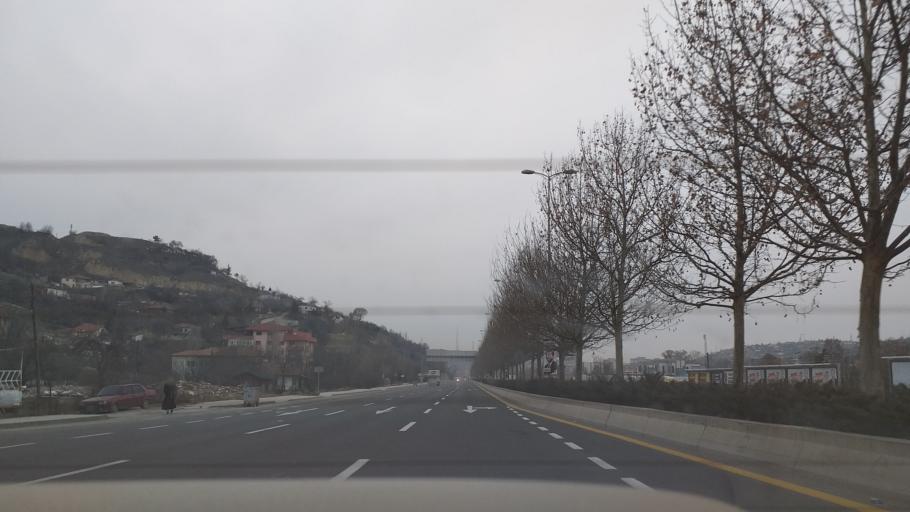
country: TR
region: Ankara
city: Mamak
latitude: 39.9125
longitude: 32.9711
